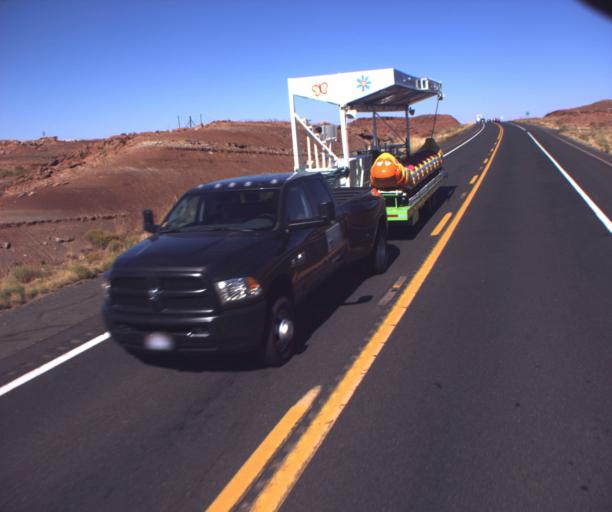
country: US
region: Arizona
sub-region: Coconino County
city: Tuba City
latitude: 35.7896
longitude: -111.4503
